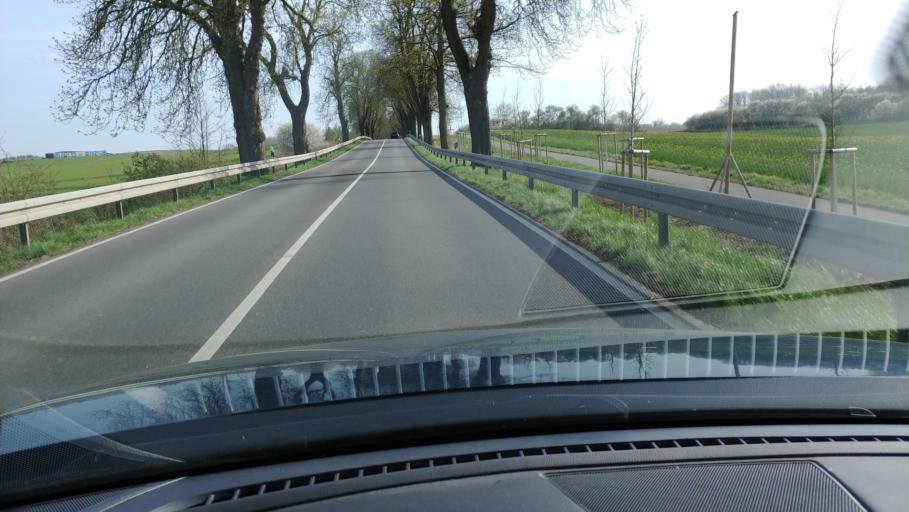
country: DE
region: Mecklenburg-Vorpommern
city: Lubstorf
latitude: 53.7008
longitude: 11.3969
